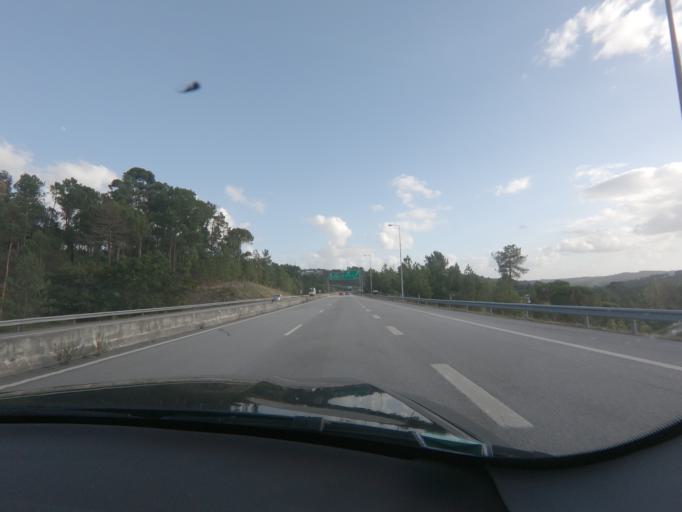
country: PT
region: Viseu
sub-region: Viseu
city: Viseu
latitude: 40.6203
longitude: -7.9630
